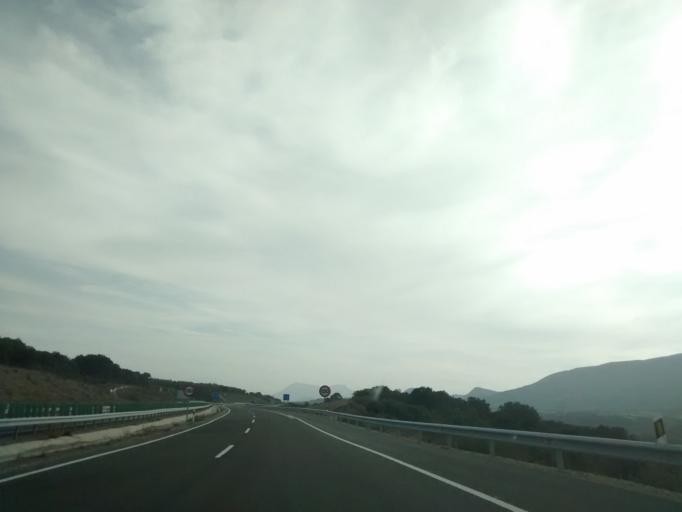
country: ES
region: Aragon
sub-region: Provincia de Zaragoza
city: Siguees
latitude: 42.6131
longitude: -0.9942
